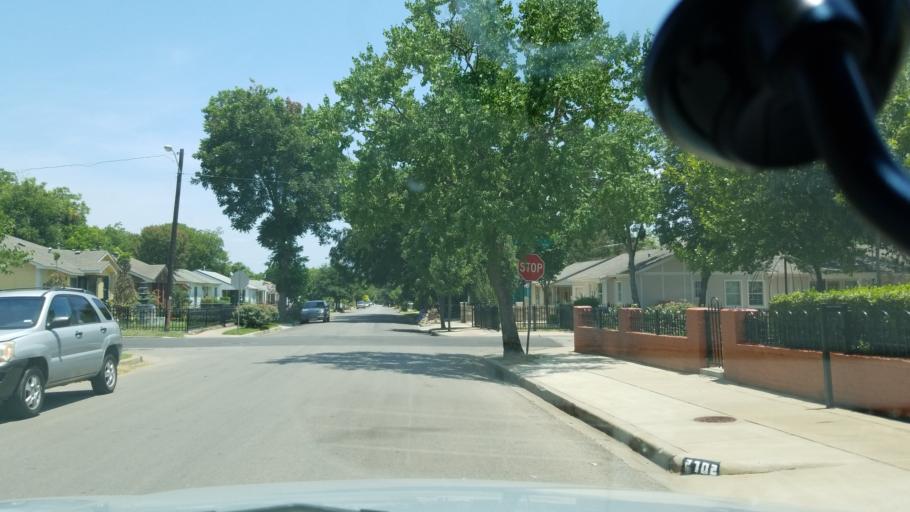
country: US
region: Texas
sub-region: Dallas County
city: Cockrell Hill
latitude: 32.7301
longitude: -96.8639
